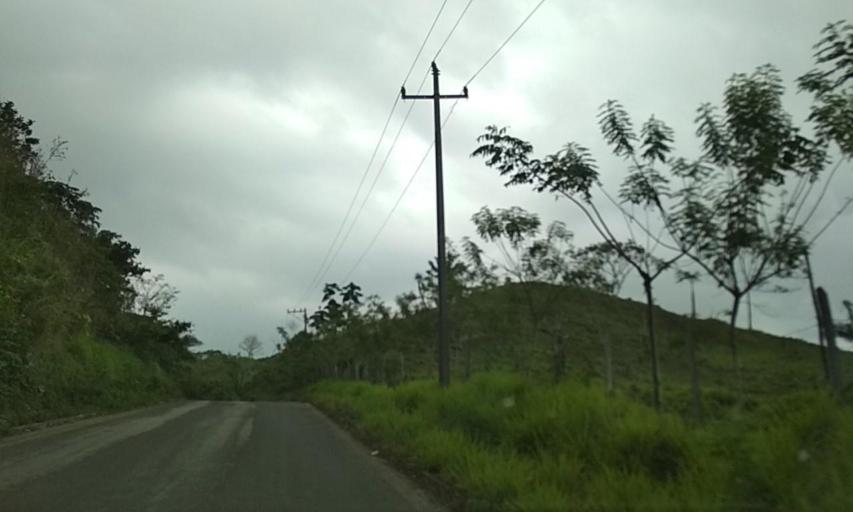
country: MX
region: Tabasco
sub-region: Huimanguillo
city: Francisco Rueda
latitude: 17.6431
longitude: -94.0933
